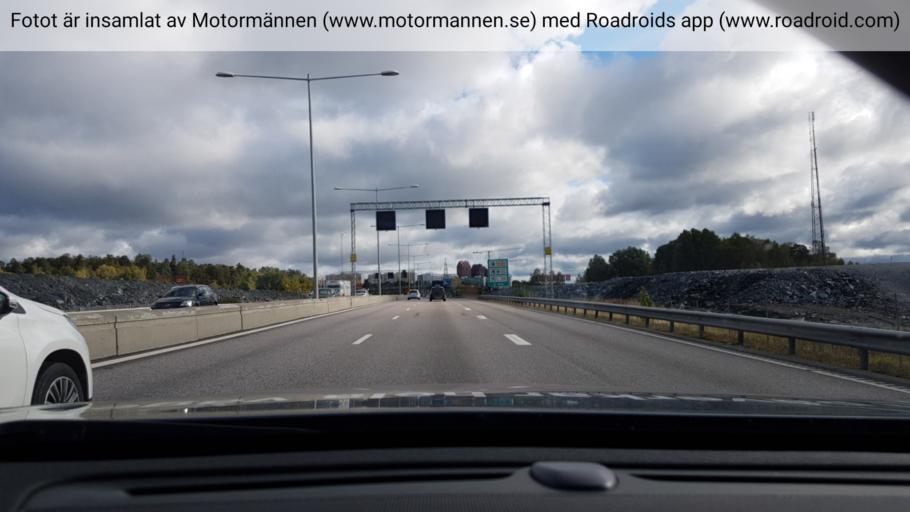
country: SE
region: Stockholm
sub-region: Botkyrka Kommun
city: Eriksberg
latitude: 59.2375
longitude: 17.8221
